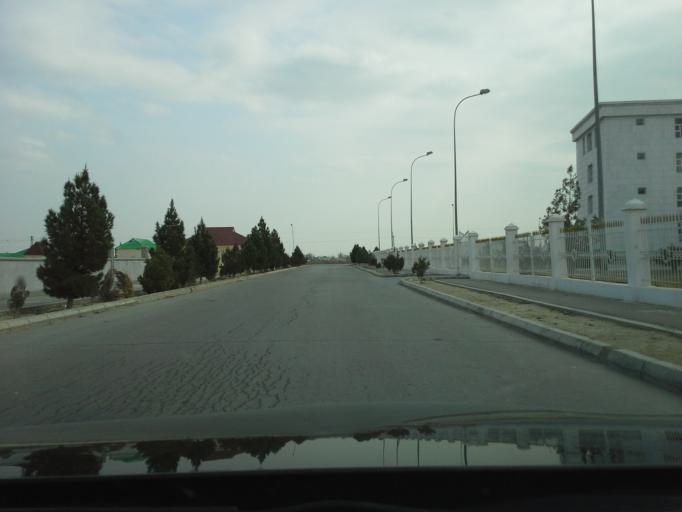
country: TM
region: Ahal
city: Abadan
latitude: 38.0362
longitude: 58.2692
